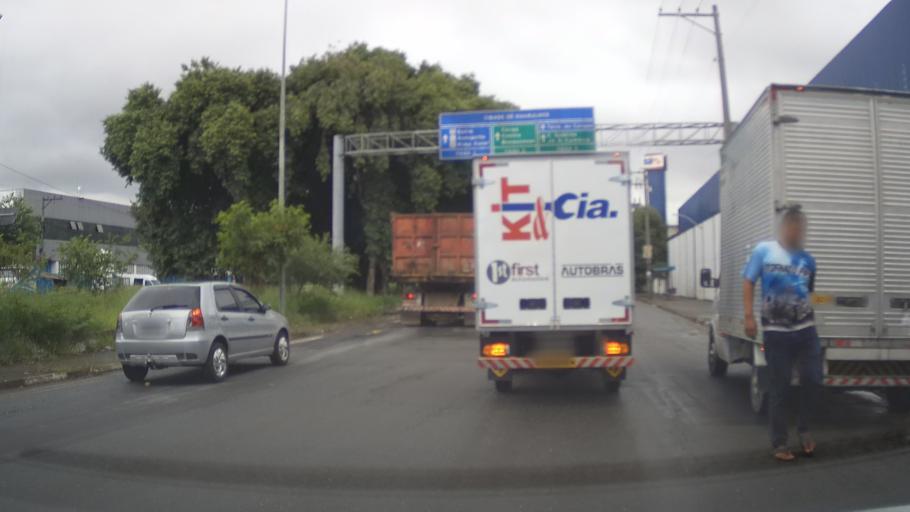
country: BR
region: Sao Paulo
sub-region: Guarulhos
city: Guarulhos
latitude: -23.4772
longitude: -46.4681
